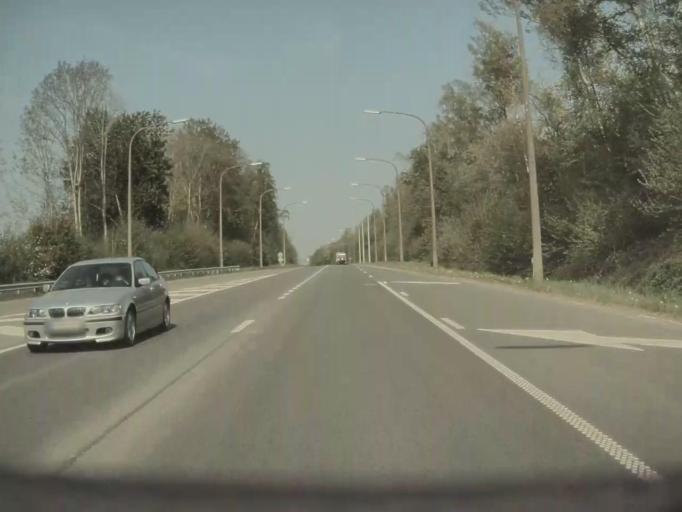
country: BE
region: Wallonia
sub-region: Province de Namur
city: Ciney
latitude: 50.2868
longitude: 5.1008
